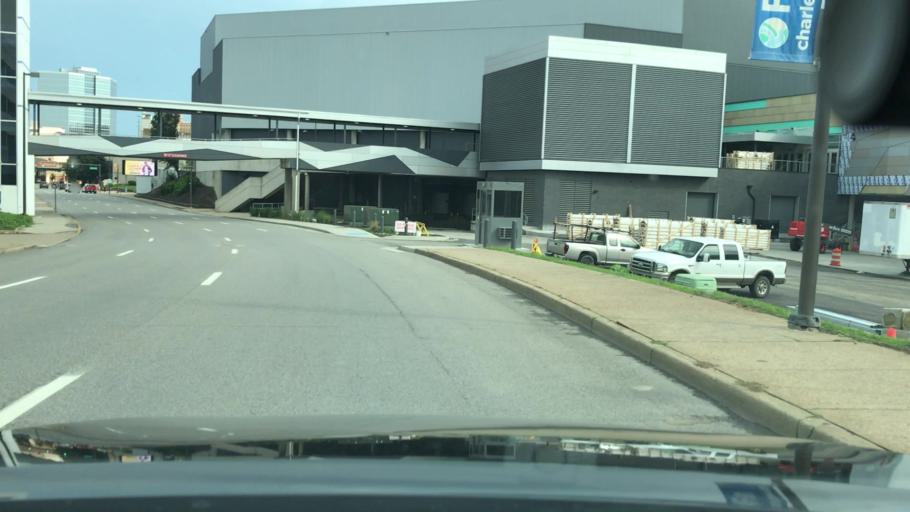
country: US
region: West Virginia
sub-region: Kanawha County
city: Charleston
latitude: 38.3571
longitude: -81.6405
